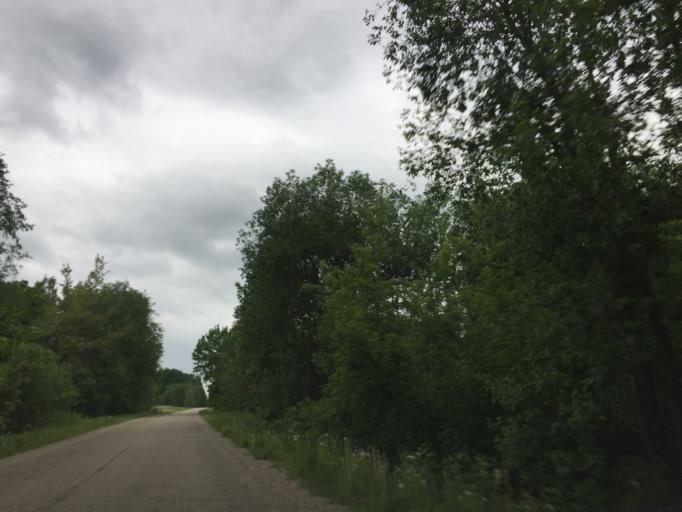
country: LV
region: Aglona
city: Aglona
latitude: 56.0815
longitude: 26.9175
